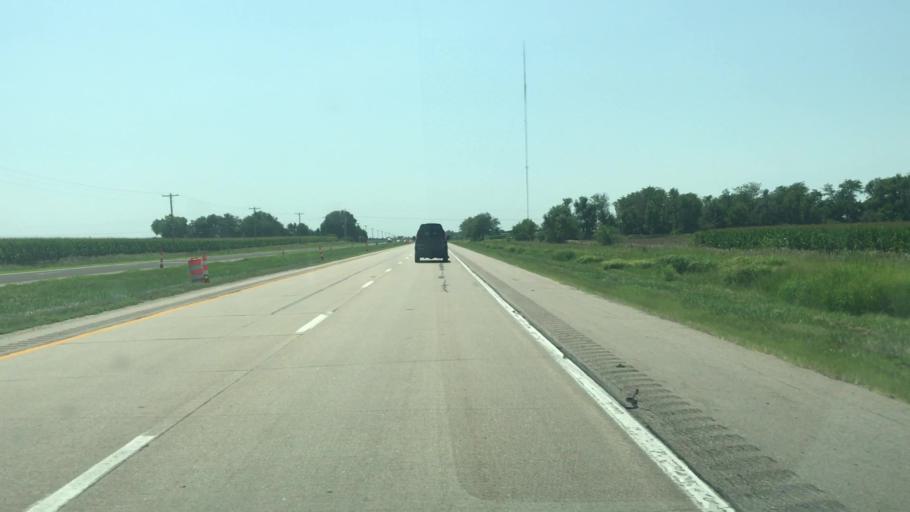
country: US
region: Nebraska
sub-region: Adams County
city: Hastings
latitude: 40.6587
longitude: -98.3824
